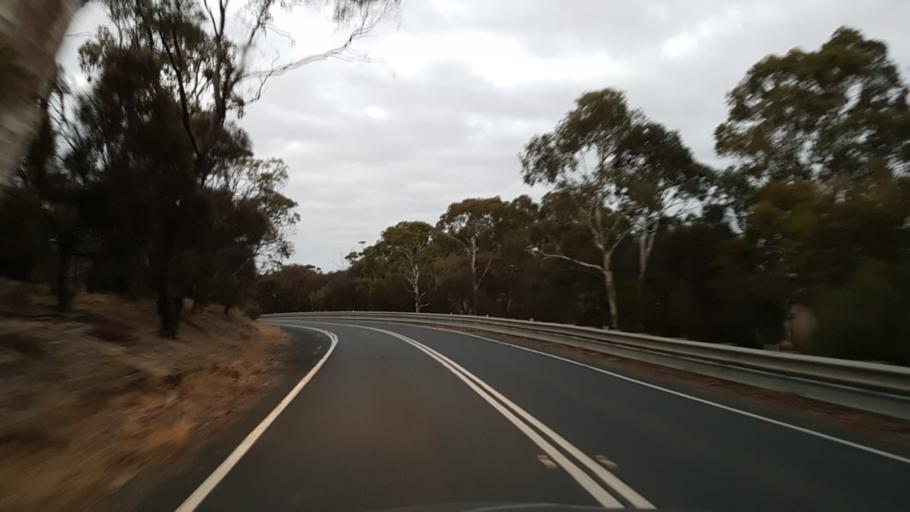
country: AU
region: South Australia
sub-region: Mount Barker
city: Callington
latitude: -35.0495
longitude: 139.0005
